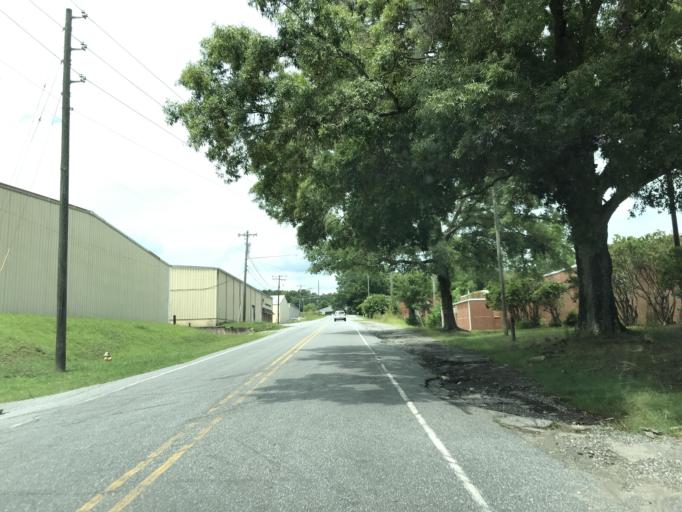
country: US
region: North Carolina
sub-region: Lincoln County
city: Lincolnton
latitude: 35.4860
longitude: -81.2516
